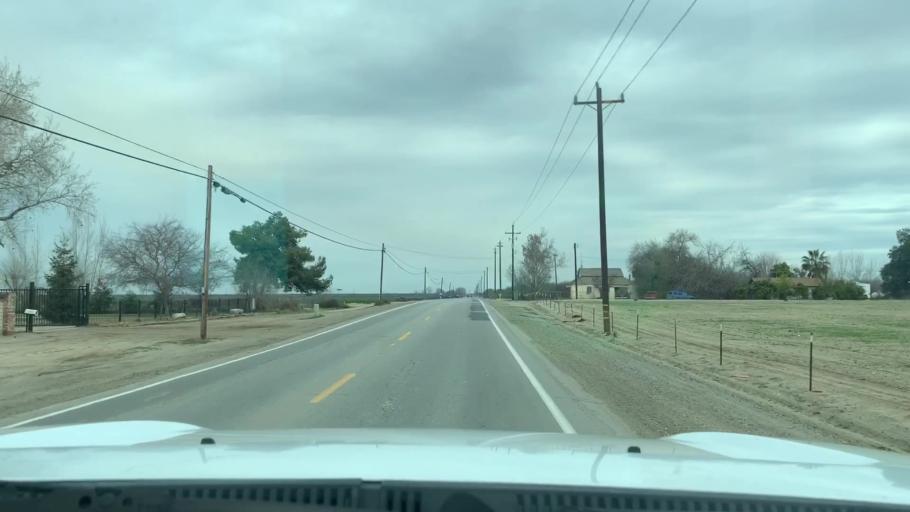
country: US
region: California
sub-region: Kern County
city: Rosedale
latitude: 35.3898
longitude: -119.2520
